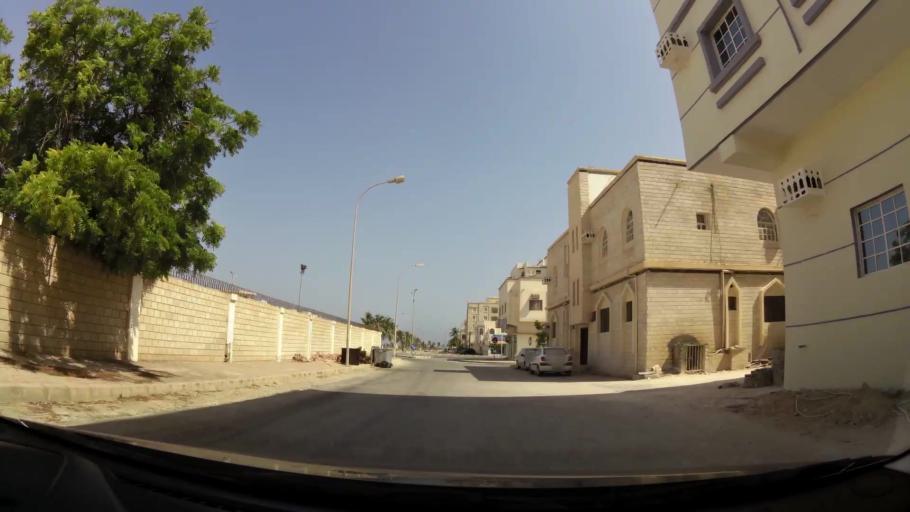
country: OM
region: Zufar
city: Salalah
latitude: 17.0071
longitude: 54.0652
